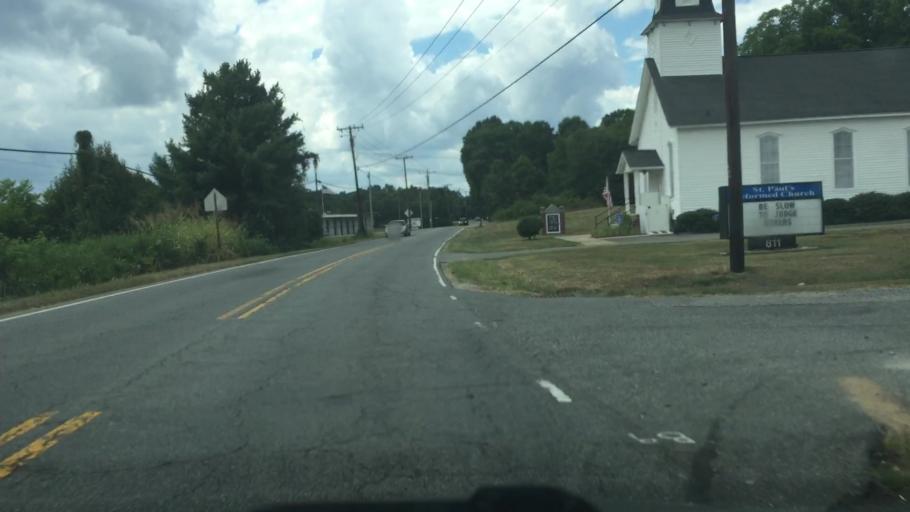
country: US
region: North Carolina
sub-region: Rowan County
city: Enochville
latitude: 35.5321
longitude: -80.6663
